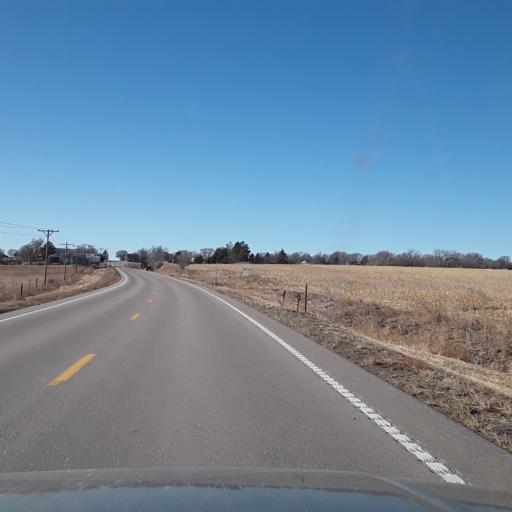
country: US
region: Nebraska
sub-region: Dawson County
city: Gothenburg
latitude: 40.7056
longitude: -100.2055
